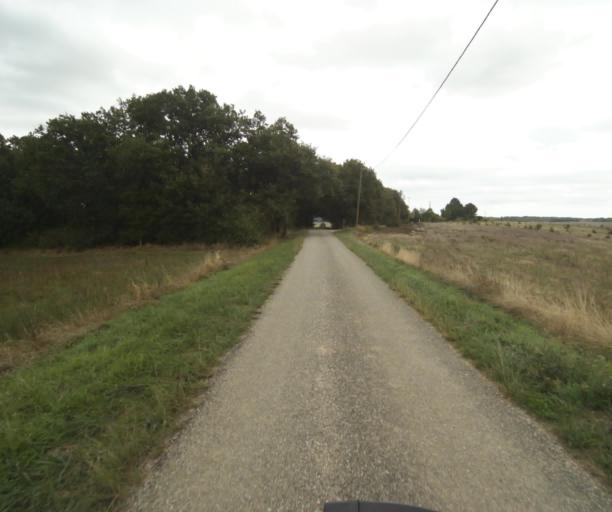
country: FR
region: Midi-Pyrenees
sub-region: Departement du Tarn-et-Garonne
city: Beaumont-de-Lomagne
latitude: 43.8555
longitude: 1.0653
